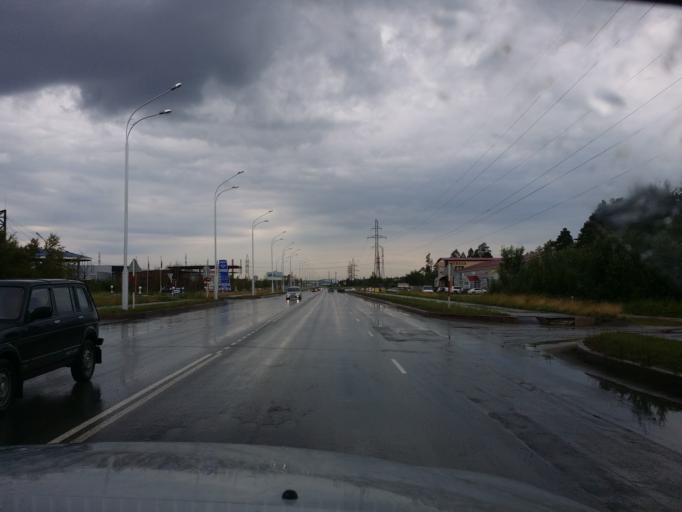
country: RU
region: Khanty-Mansiyskiy Avtonomnyy Okrug
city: Nizhnevartovsk
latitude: 60.9624
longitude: 76.5552
